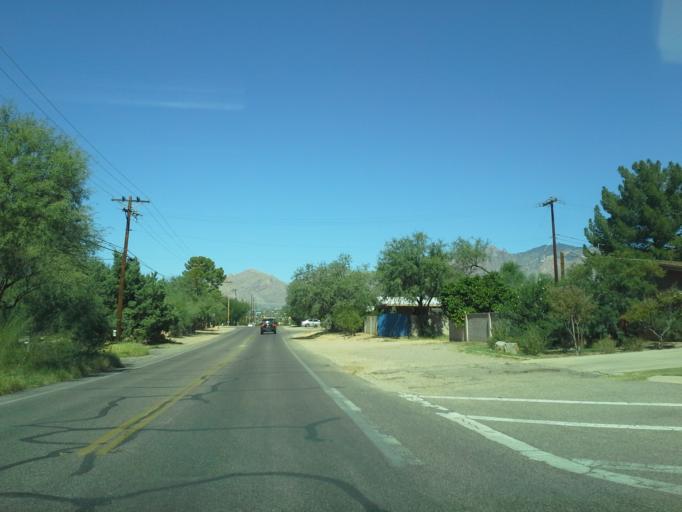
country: US
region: Arizona
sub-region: Pima County
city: Catalina Foothills
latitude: 32.2691
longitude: -110.9352
